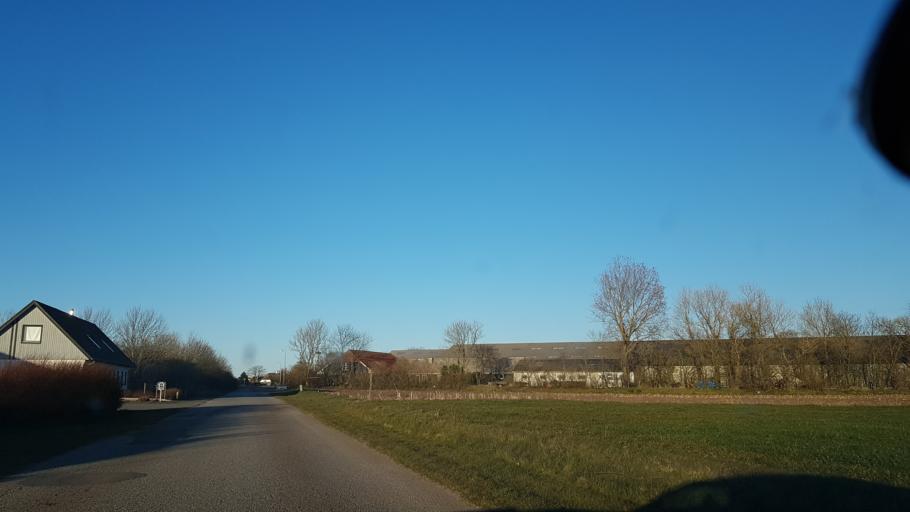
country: DK
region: South Denmark
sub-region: Esbjerg Kommune
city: Ribe
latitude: 55.3902
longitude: 8.7166
